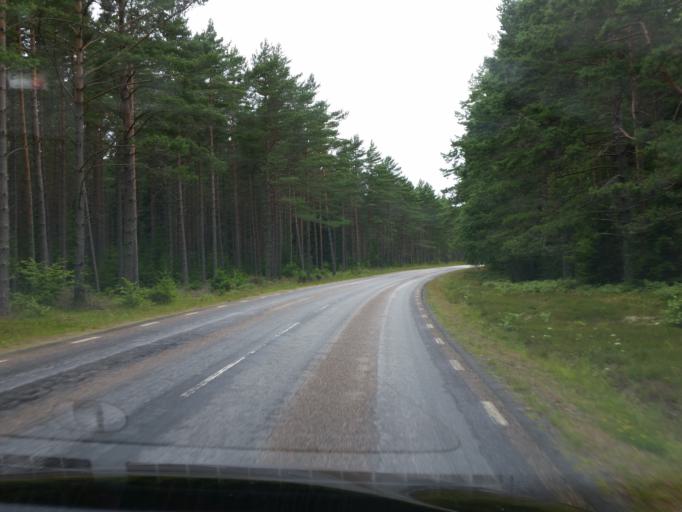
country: SE
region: Soedermanland
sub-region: Trosa Kommun
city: Trosa
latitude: 58.7650
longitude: 17.3441
